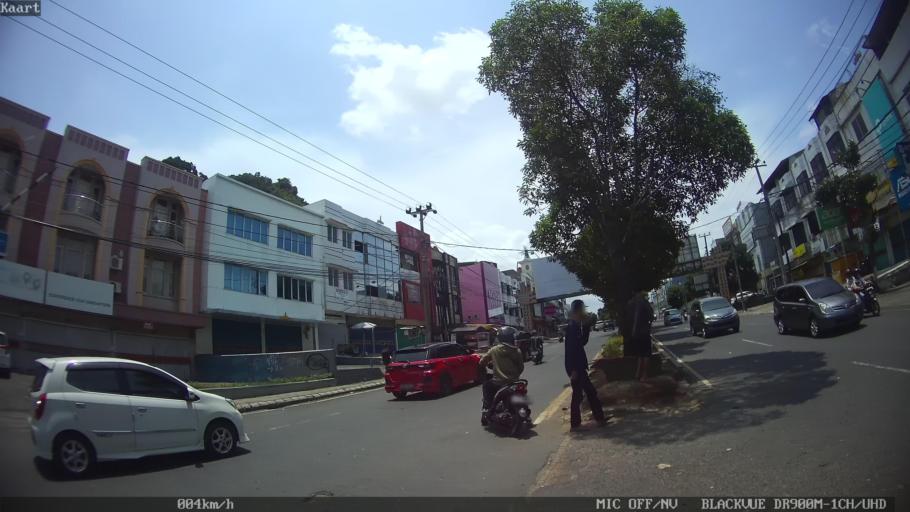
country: ID
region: Lampung
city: Kedaton
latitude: -5.3909
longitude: 105.2620
